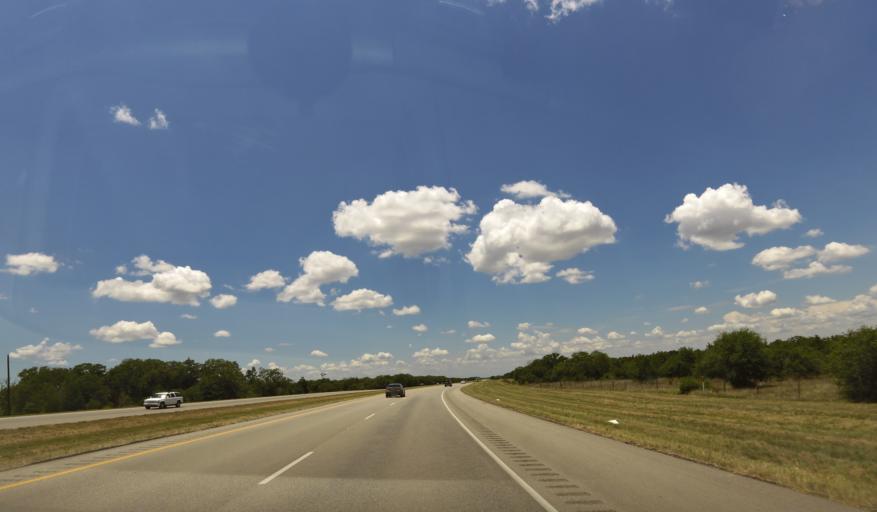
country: US
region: Texas
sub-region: Lee County
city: Giddings
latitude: 30.1409
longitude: -96.7656
